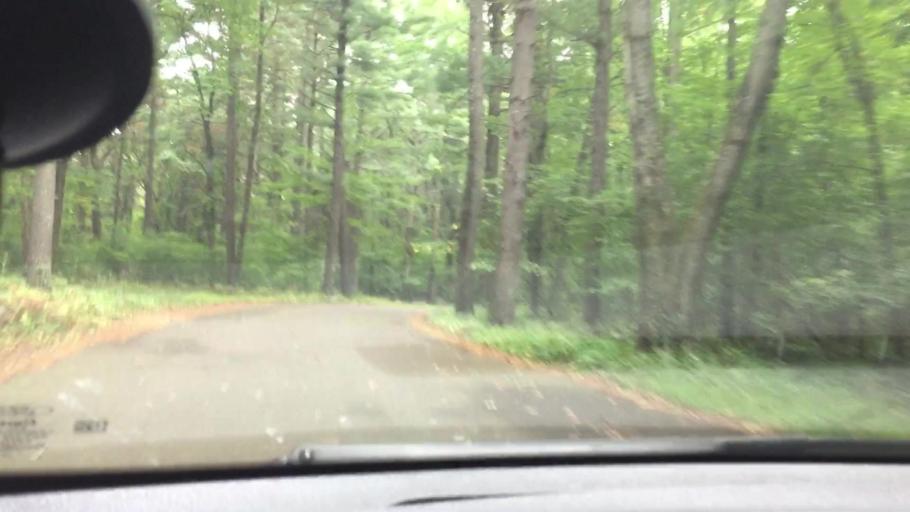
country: US
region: Wisconsin
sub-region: Chippewa County
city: Chippewa Falls
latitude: 44.9595
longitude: -91.4014
